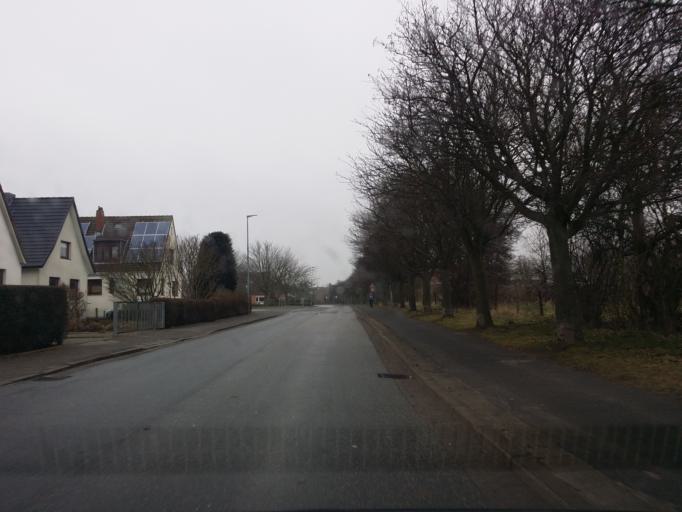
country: DE
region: Schleswig-Holstein
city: Burg auf Fehmarn
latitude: 54.4307
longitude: 11.2006
